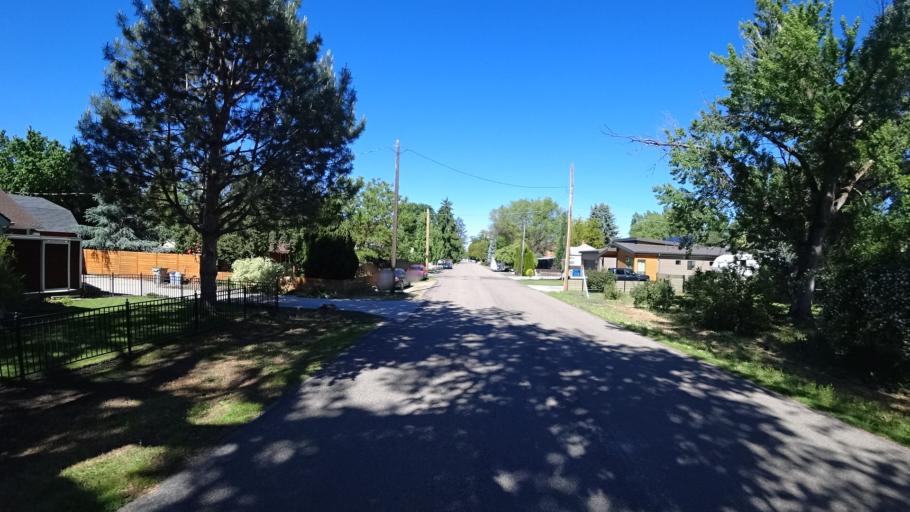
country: US
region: Idaho
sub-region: Ada County
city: Garden City
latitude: 43.6426
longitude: -116.2188
